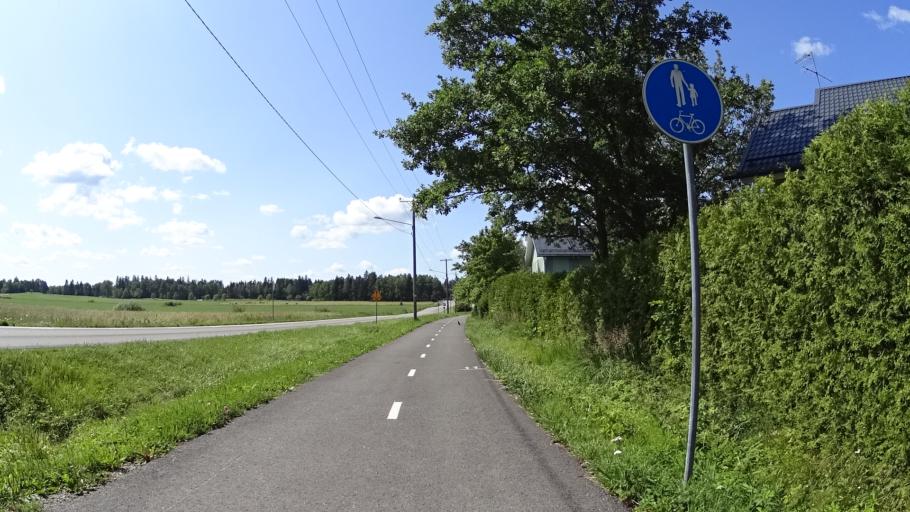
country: FI
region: Uusimaa
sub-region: Helsinki
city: Jaervenpaeae
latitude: 60.4643
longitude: 25.0642
